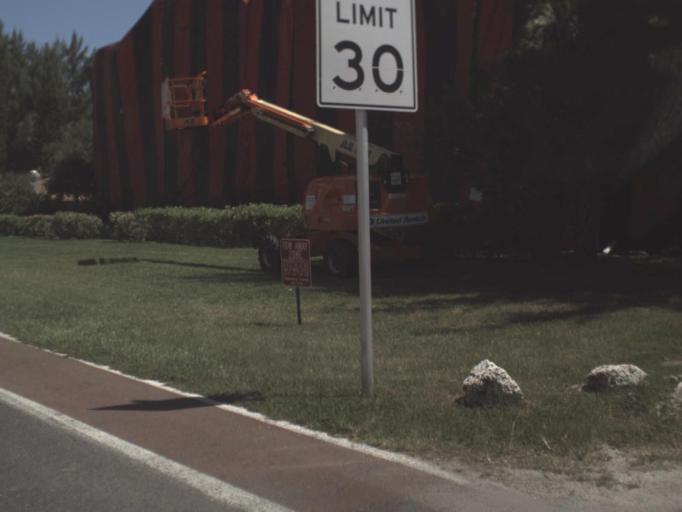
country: US
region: Florida
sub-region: Pinellas County
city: Indian Shores
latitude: 27.8462
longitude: -82.8424
